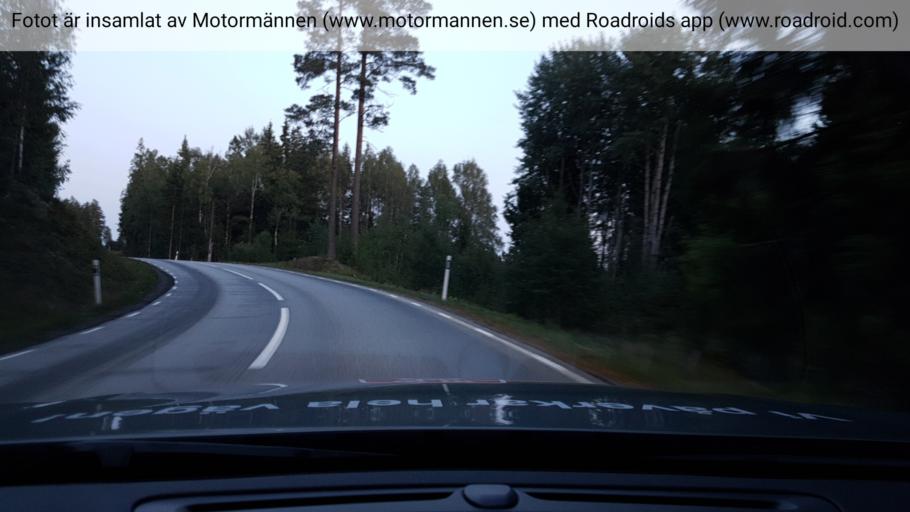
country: SE
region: OErebro
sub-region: Ljusnarsbergs Kommun
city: Kopparberg
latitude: 59.8050
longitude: 14.8484
